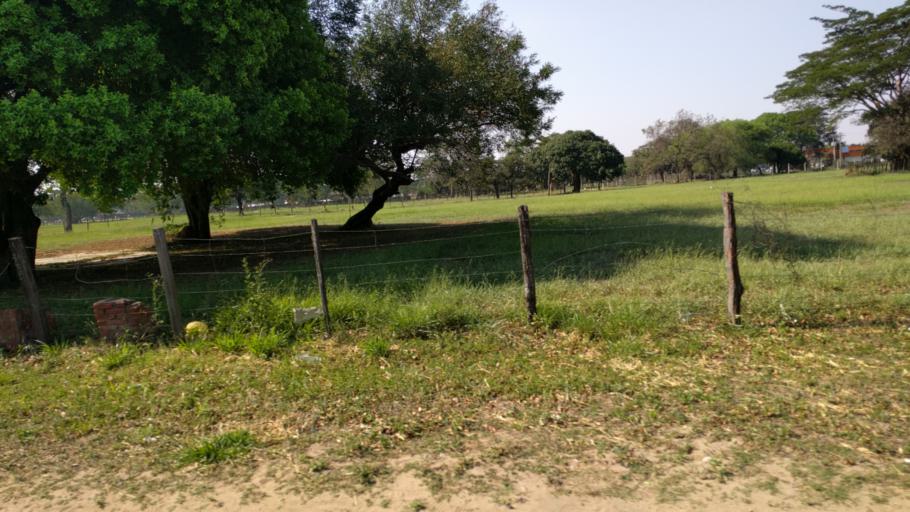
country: BO
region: Santa Cruz
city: Santa Cruz de la Sierra
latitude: -17.8125
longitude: -63.1642
